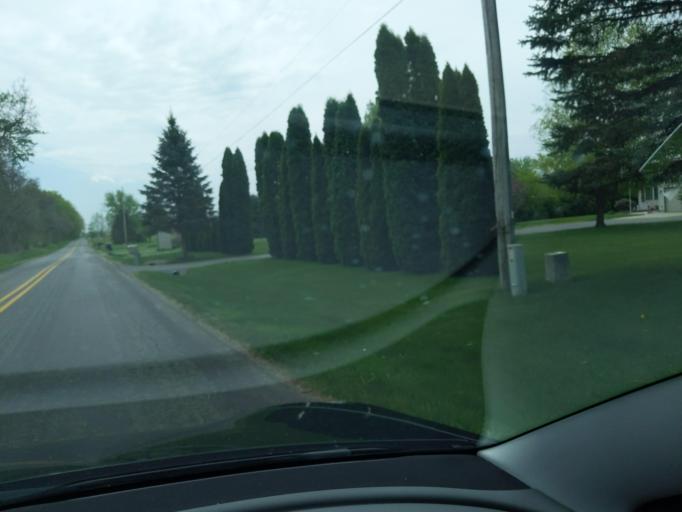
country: US
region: Michigan
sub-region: Ingham County
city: Holt
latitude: 42.5497
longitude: -84.5424
